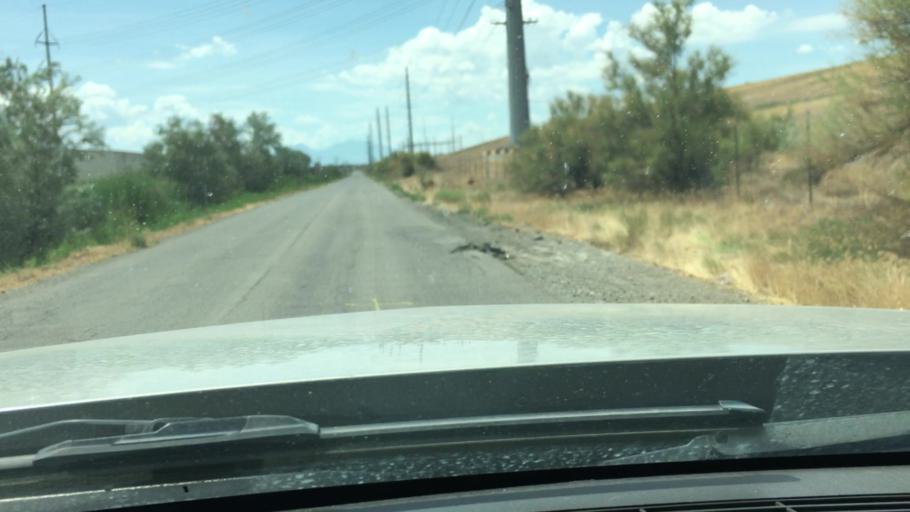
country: US
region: Utah
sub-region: Utah County
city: Pleasant Grove
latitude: 40.3381
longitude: -111.7599
